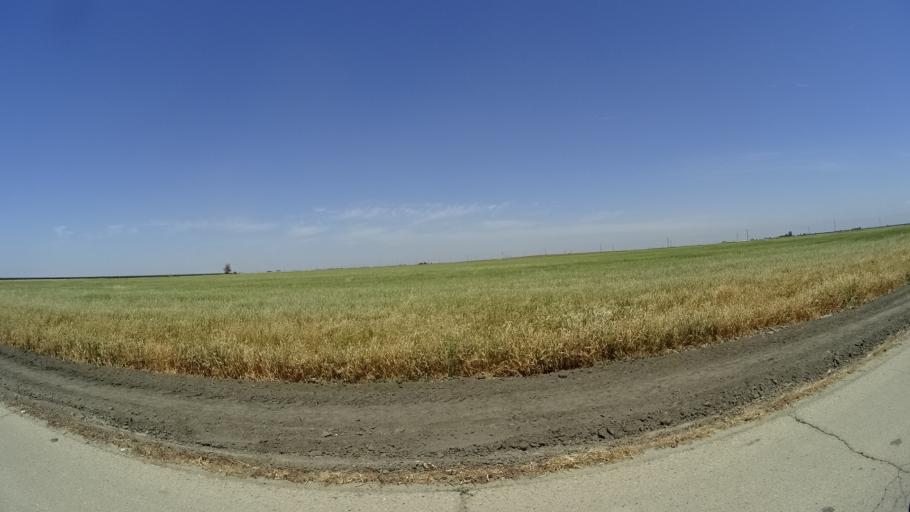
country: US
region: California
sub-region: Kings County
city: Corcoran
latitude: 36.1198
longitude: -119.5791
